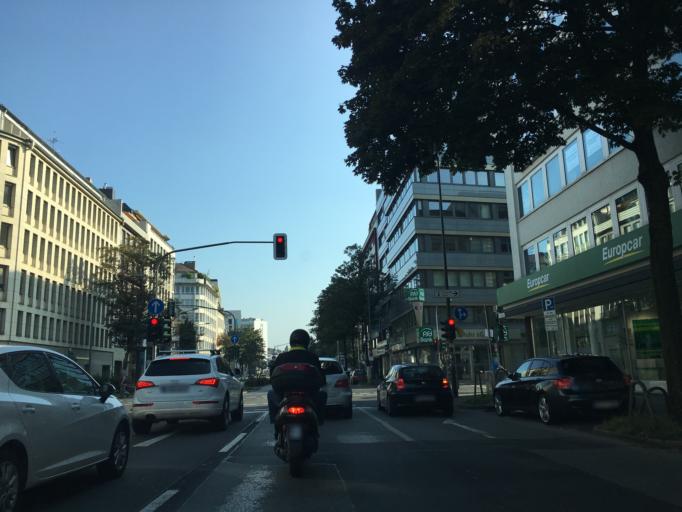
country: DE
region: North Rhine-Westphalia
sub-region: Regierungsbezirk Dusseldorf
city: Dusseldorf
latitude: 51.2204
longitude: 6.7895
